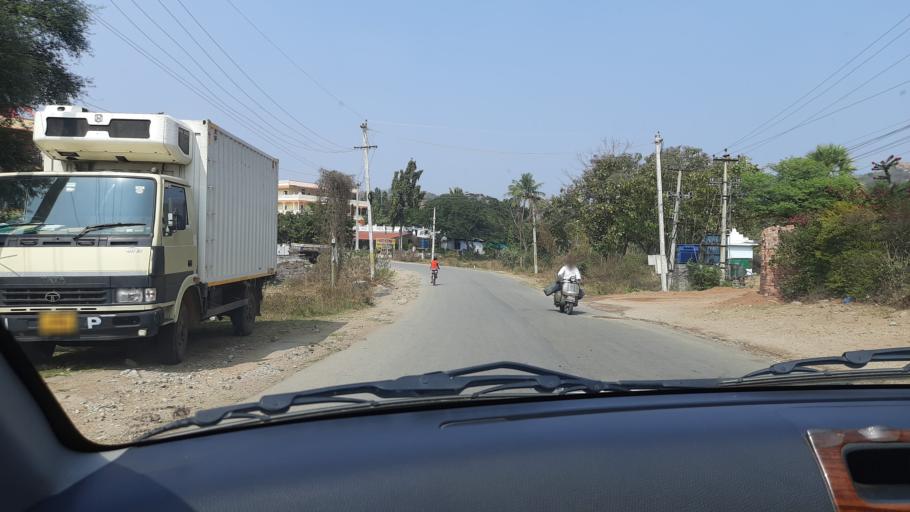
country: IN
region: Telangana
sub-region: Rangareddi
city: Lal Bahadur Nagar
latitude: 17.2724
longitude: 78.6693
